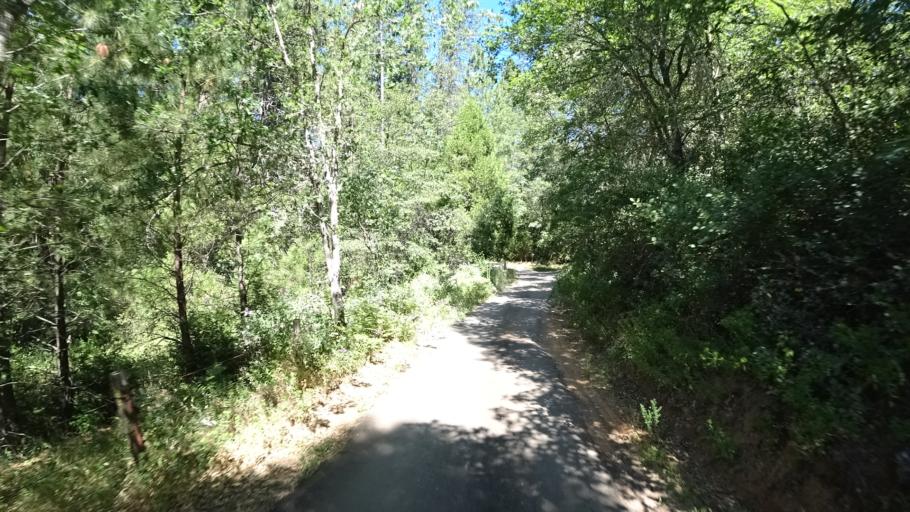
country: US
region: California
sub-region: Amador County
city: Pioneer
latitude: 38.3863
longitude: -120.4975
